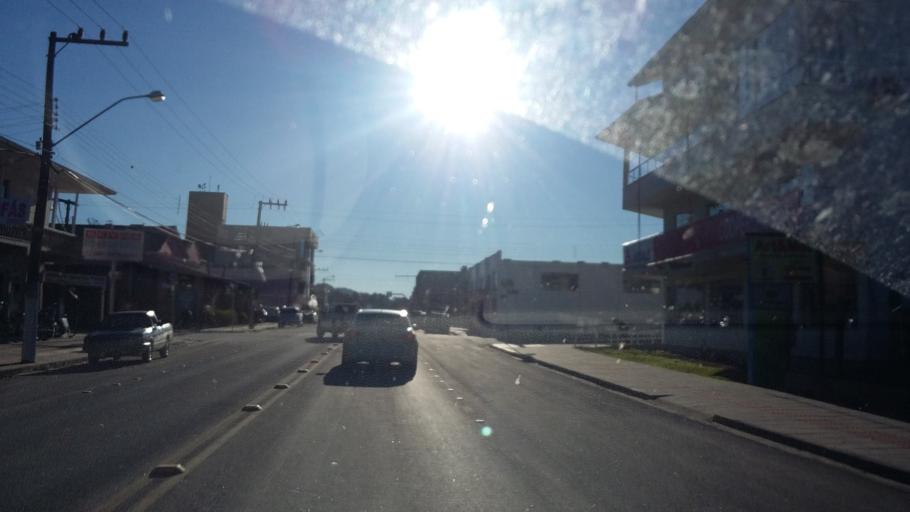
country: BR
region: Santa Catarina
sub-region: Lauro Muller
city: Lauro Muller
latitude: -27.9909
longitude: -49.5812
